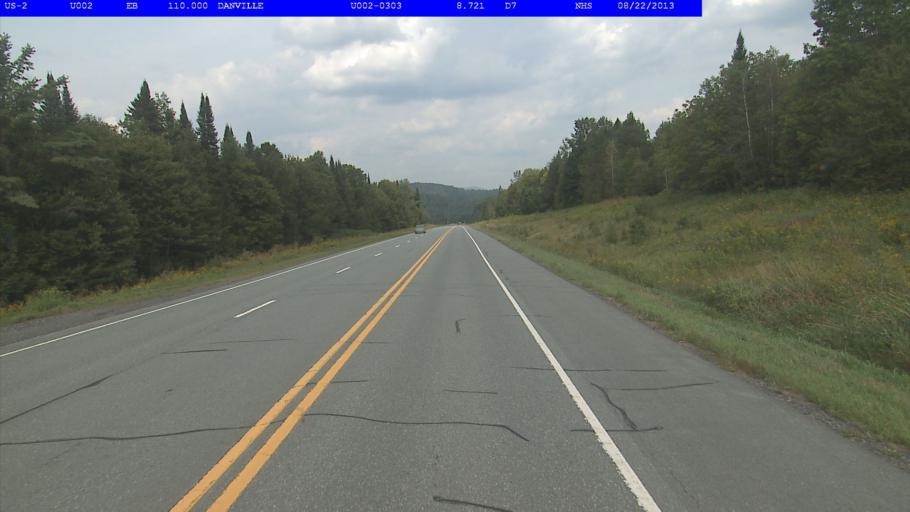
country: US
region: Vermont
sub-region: Caledonia County
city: St Johnsbury
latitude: 44.4408
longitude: -72.0667
